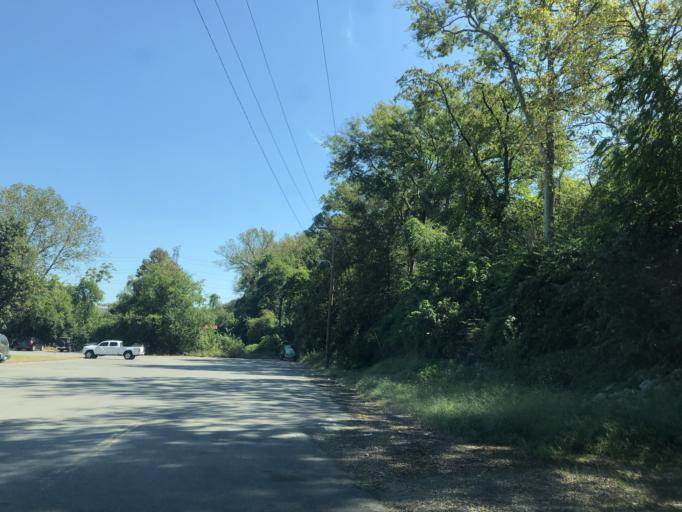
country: US
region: Tennessee
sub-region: Davidson County
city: Nashville
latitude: 36.1395
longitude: -86.7603
